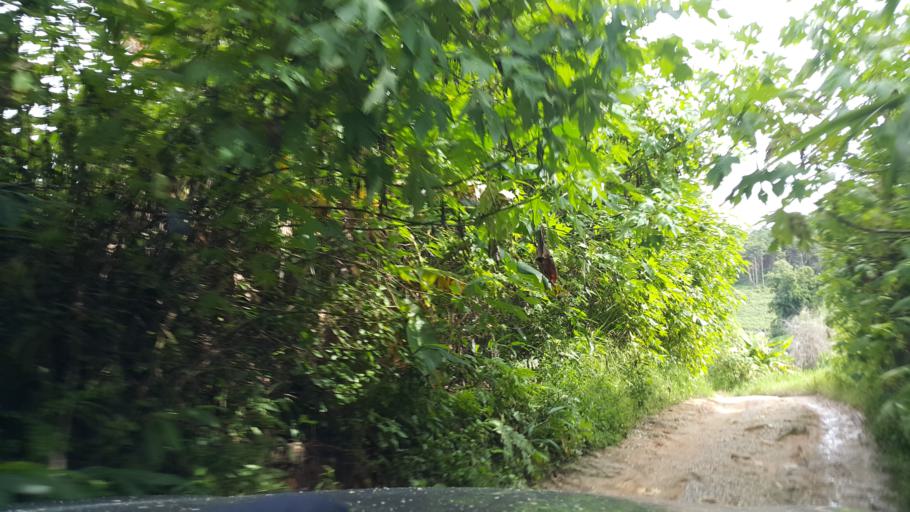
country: TH
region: Chiang Mai
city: Samoeng
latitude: 18.8716
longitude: 98.5009
